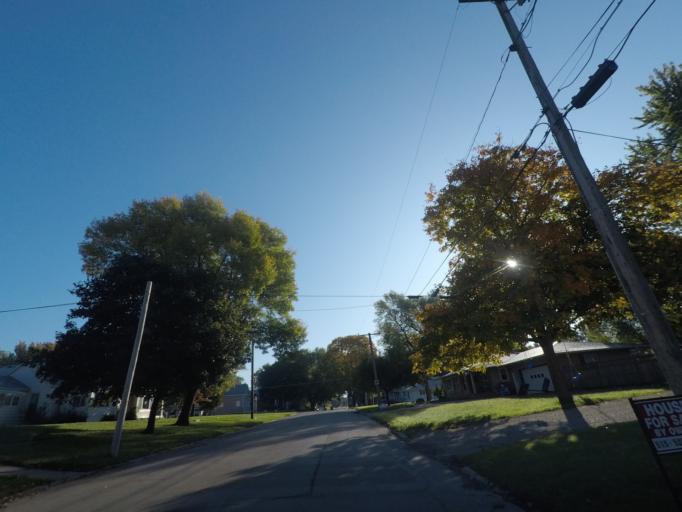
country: US
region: Iowa
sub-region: Story County
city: Nevada
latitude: 42.0196
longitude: -93.4572
